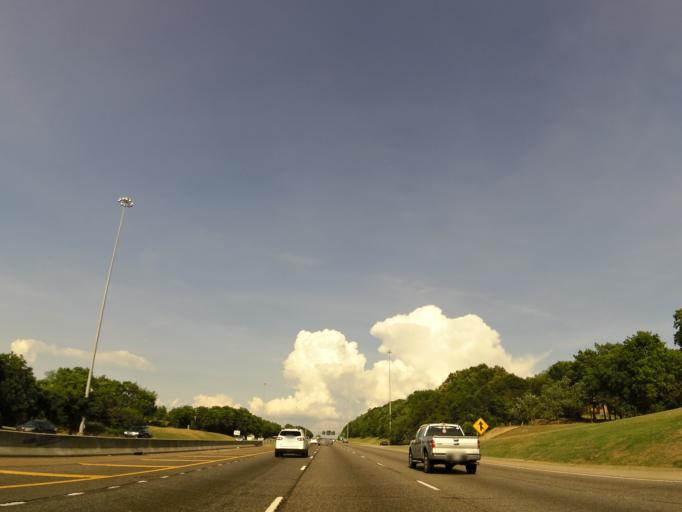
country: US
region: Alabama
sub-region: Jefferson County
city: Birmingham
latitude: 33.5209
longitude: -86.8484
